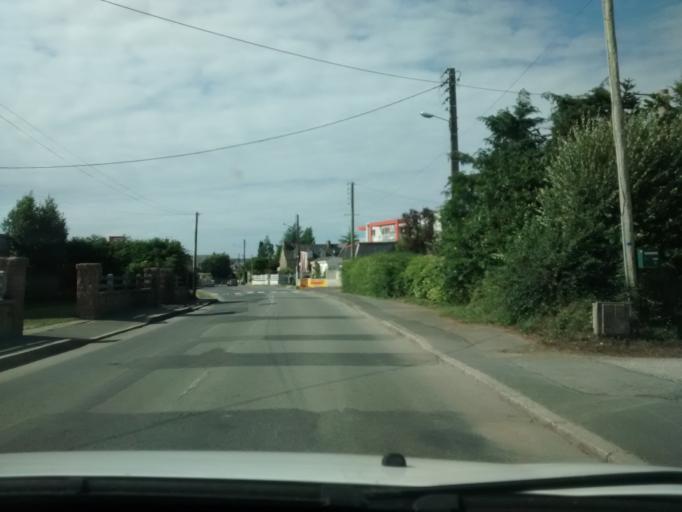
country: FR
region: Brittany
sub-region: Departement des Cotes-d'Armor
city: Penvenan
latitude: 48.8077
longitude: -3.2941
